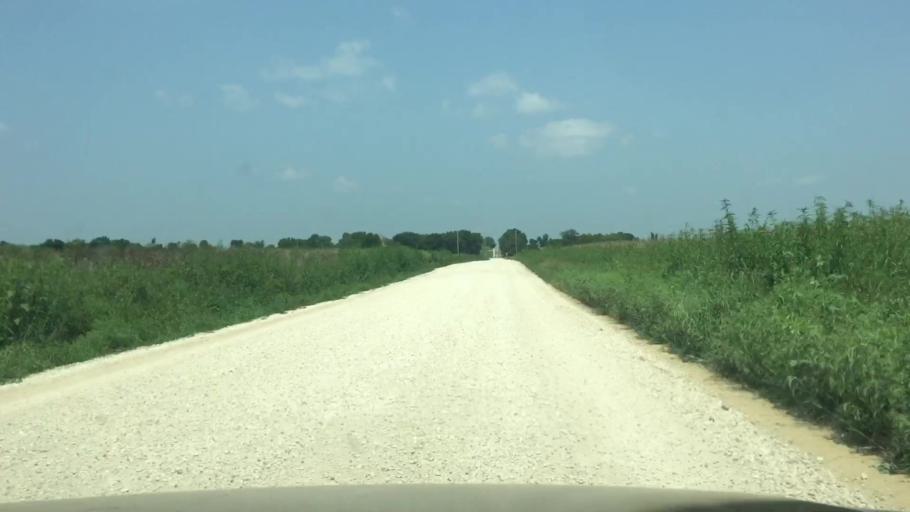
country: US
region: Kansas
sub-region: Allen County
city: Iola
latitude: 37.8742
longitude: -95.3911
